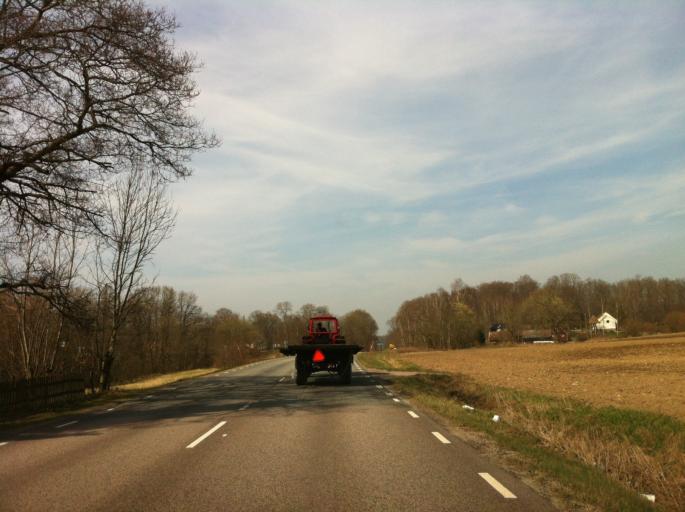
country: SE
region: Skane
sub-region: Klippans Kommun
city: Ljungbyhed
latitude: 55.9971
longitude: 13.2991
